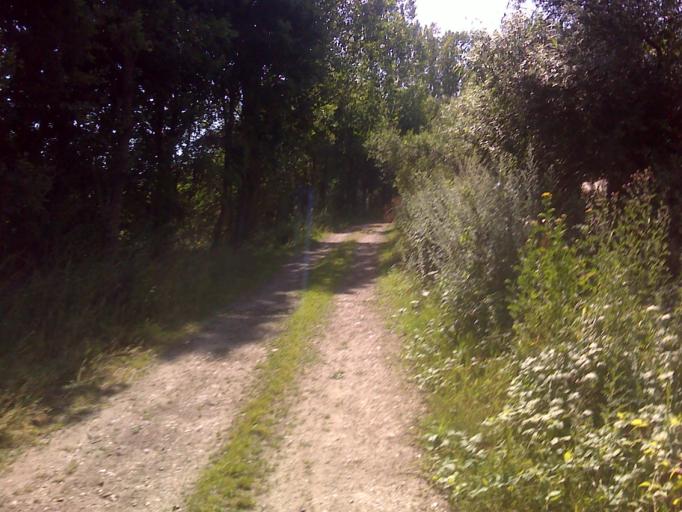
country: NL
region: Limburg
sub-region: Gemeente Maasgouw
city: Maasbracht
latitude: 51.1525
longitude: 5.8398
